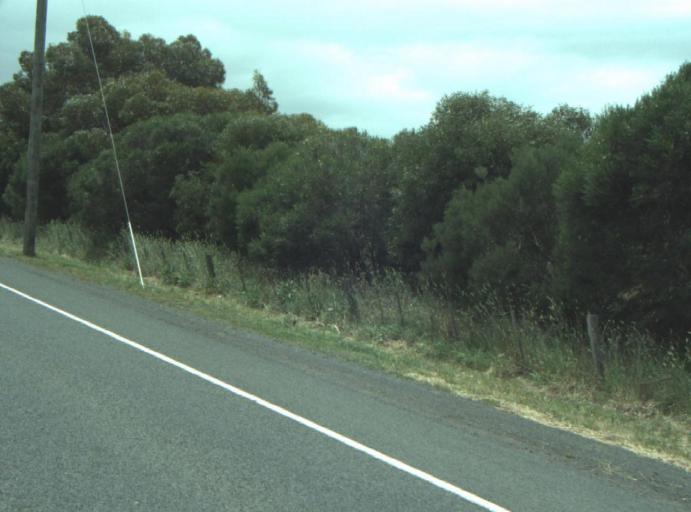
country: AU
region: Victoria
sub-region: Greater Geelong
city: Wandana Heights
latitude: -38.2384
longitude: 144.2787
